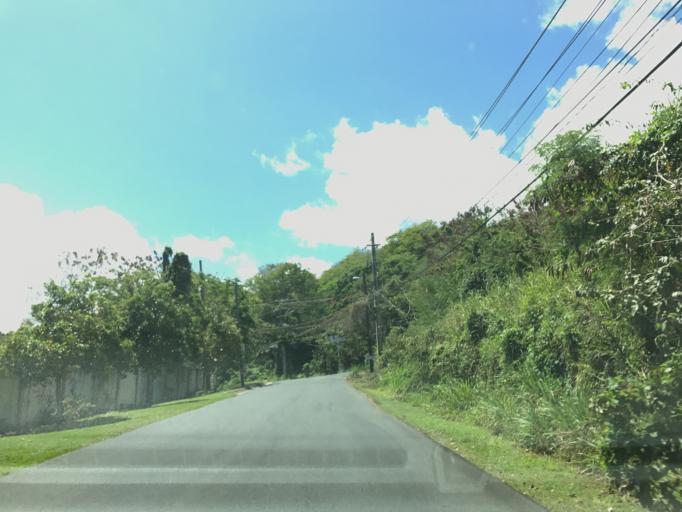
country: PR
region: Rio Grande
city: Palmer
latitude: 18.3845
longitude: -65.7671
